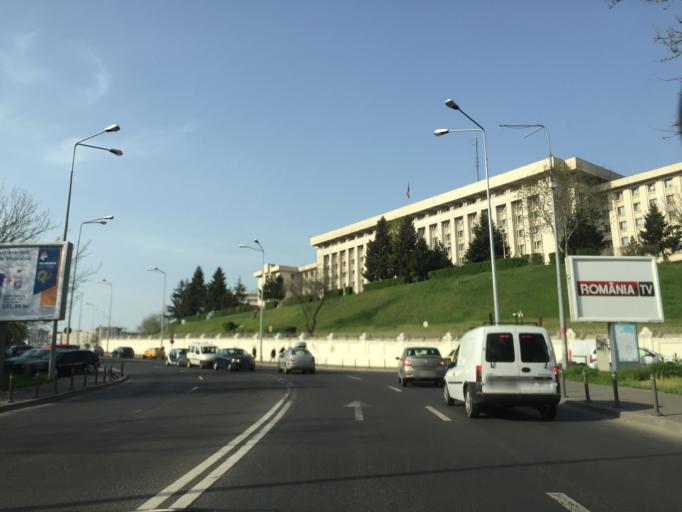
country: RO
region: Bucuresti
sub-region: Municipiul Bucuresti
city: Bucuresti
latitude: 44.4287
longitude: 26.0797
